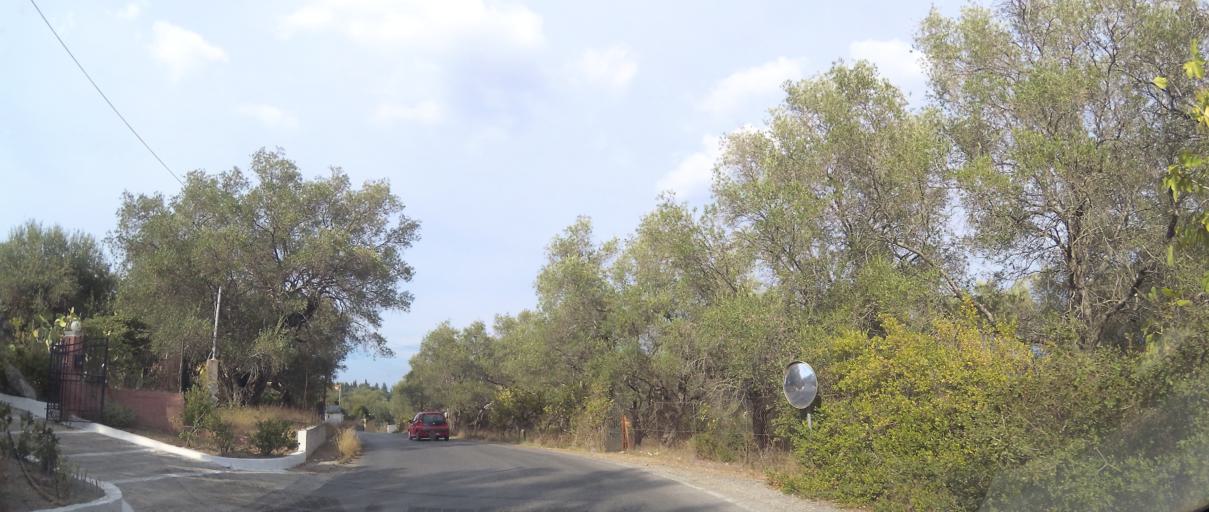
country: GR
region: Ionian Islands
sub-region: Nomos Kerkyras
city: Kynopiastes
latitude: 39.5594
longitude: 19.8621
